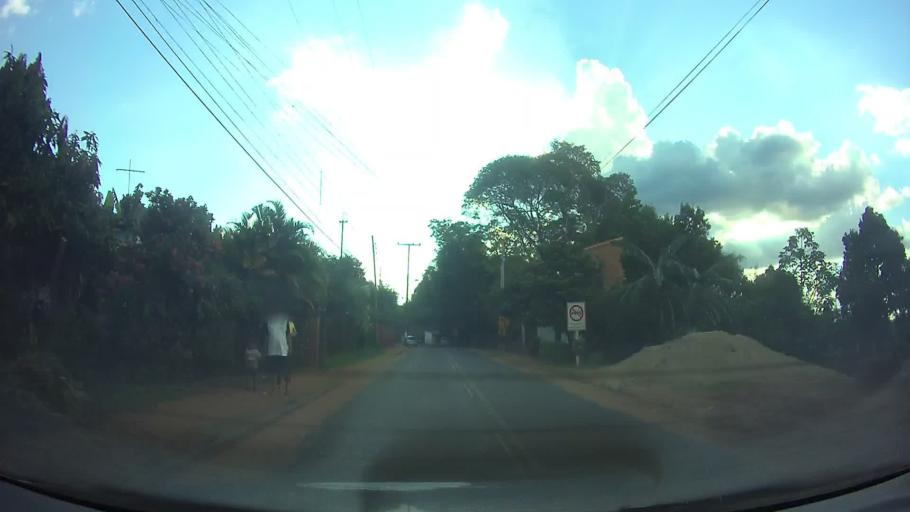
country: PY
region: Central
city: Aregua
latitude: -25.2835
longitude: -57.4362
